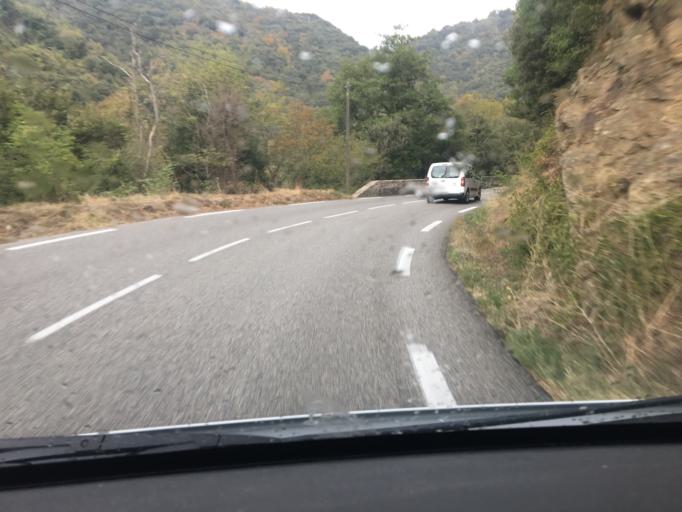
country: FR
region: Rhone-Alpes
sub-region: Departement de l'Ardeche
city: Saint-Jean-de-Muzols
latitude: 45.0644
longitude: 4.7815
